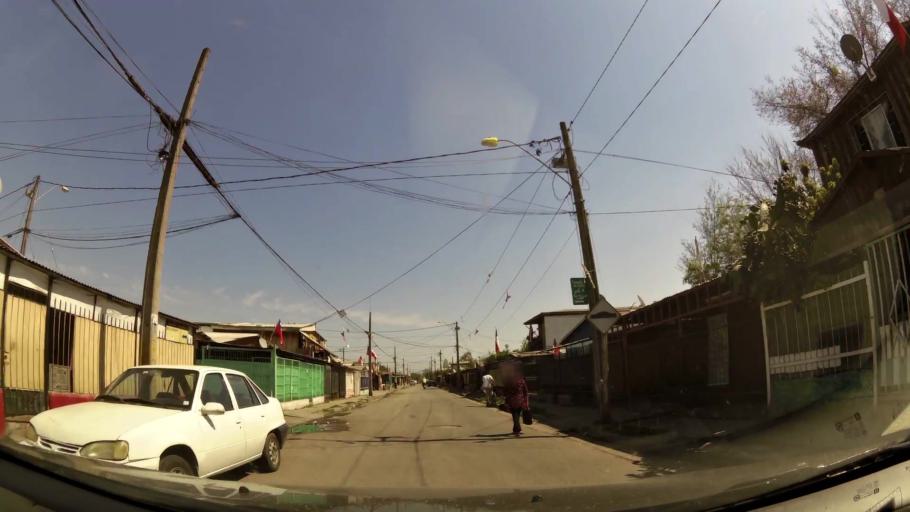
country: CL
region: Santiago Metropolitan
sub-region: Provincia de Santiago
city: La Pintana
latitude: -33.5884
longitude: -70.6212
